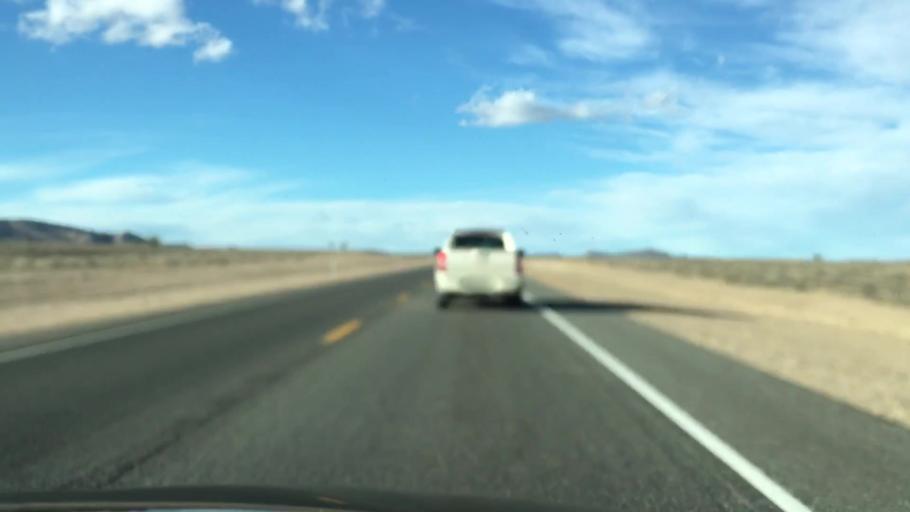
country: US
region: Nevada
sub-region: Esmeralda County
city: Goldfield
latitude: 37.5759
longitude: -117.2033
